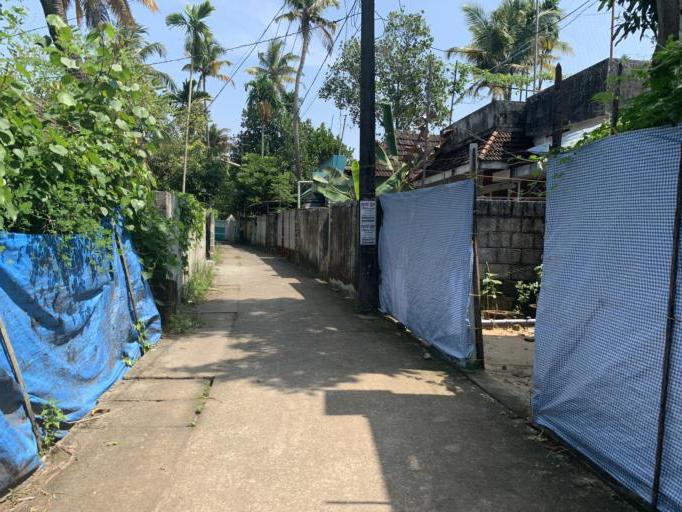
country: IN
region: Kerala
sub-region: Ernakulam
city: Cochin
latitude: 9.9756
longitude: 76.2403
